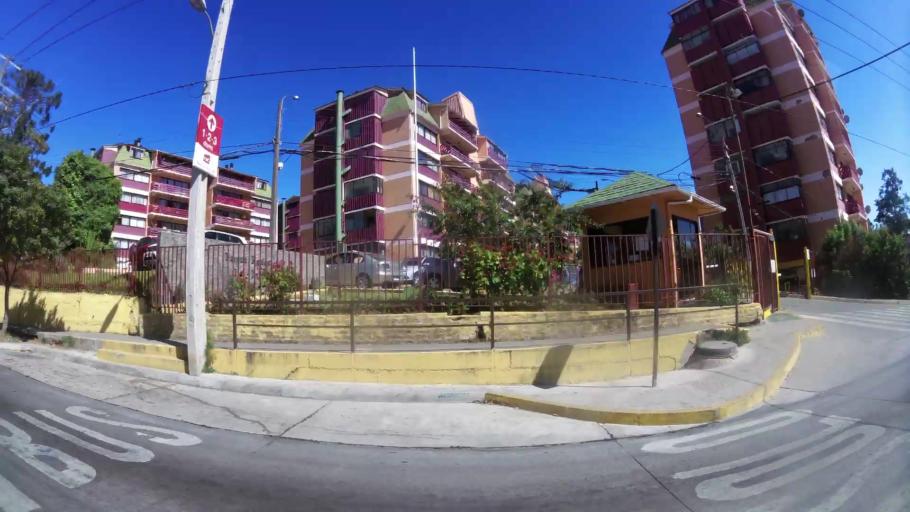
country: CL
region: Valparaiso
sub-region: Provincia de Valparaiso
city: Valparaiso
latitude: -33.0564
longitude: -71.5858
